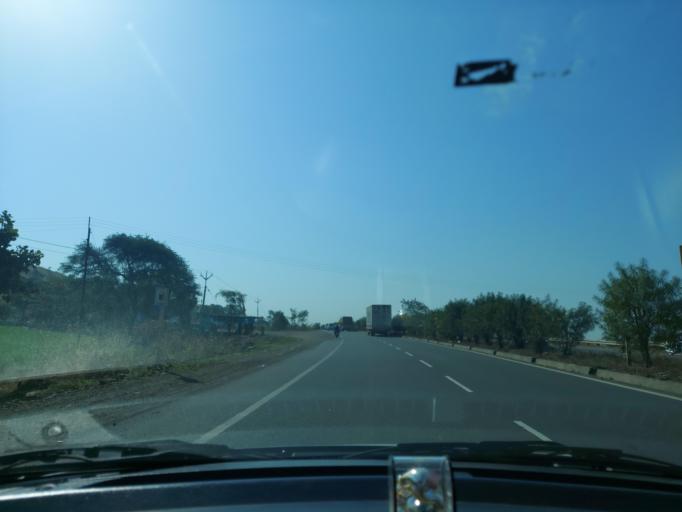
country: IN
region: Madhya Pradesh
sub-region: Indore
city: Pithampur
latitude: 22.5741
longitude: 75.6467
